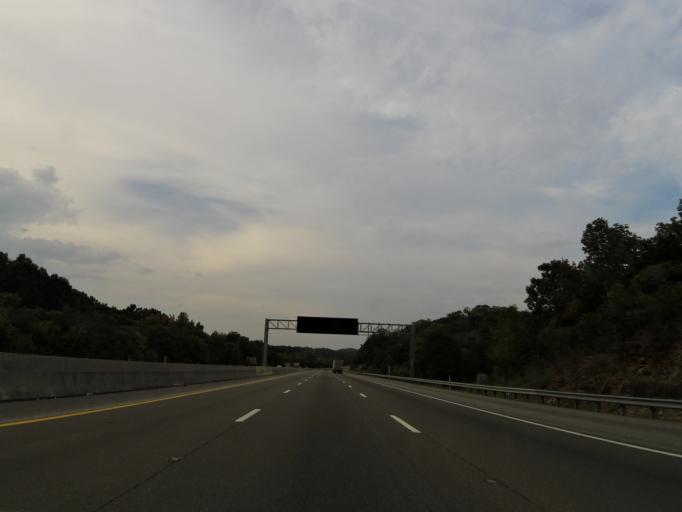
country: US
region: Tennessee
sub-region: Davidson County
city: Belle Meade
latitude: 36.0969
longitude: -86.9364
